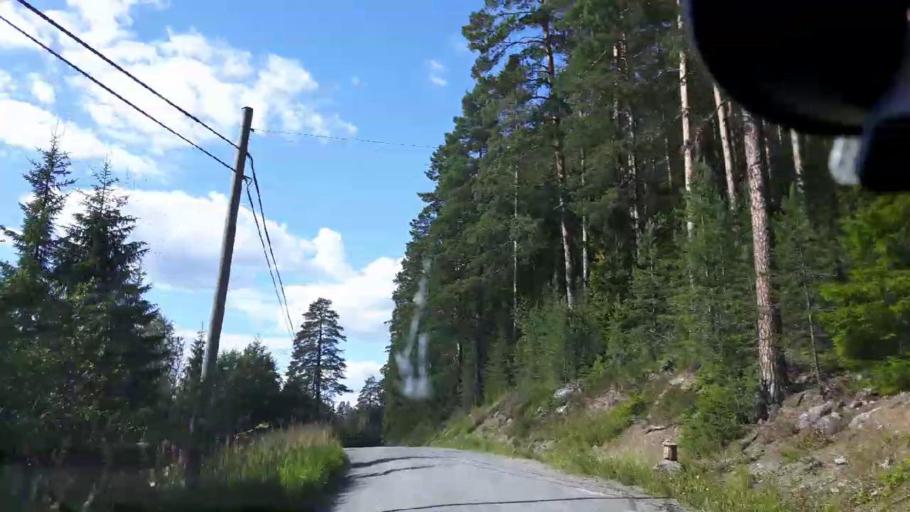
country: SE
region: Jaemtland
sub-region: Braecke Kommun
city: Braecke
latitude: 62.8597
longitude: 15.2789
